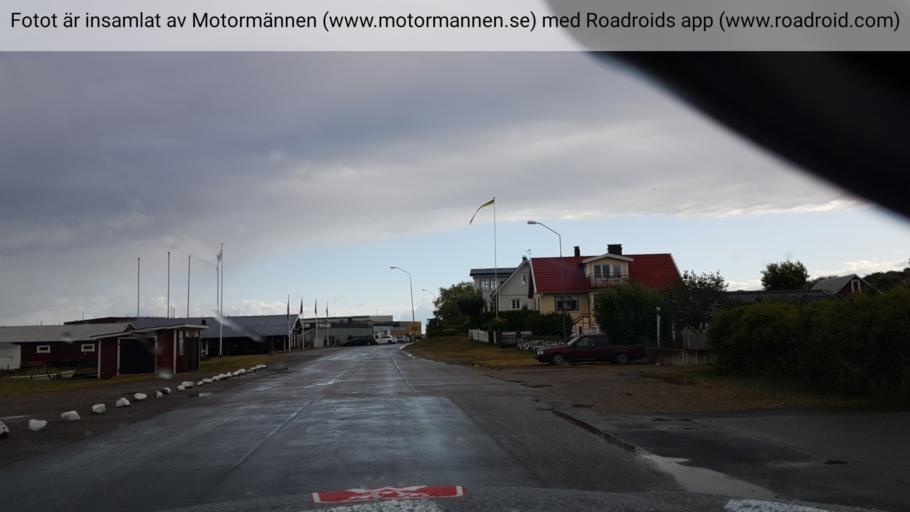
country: SE
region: Blekinge
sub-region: Solvesborgs Kommun
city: Soelvesborg
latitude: 56.0118
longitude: 14.6972
